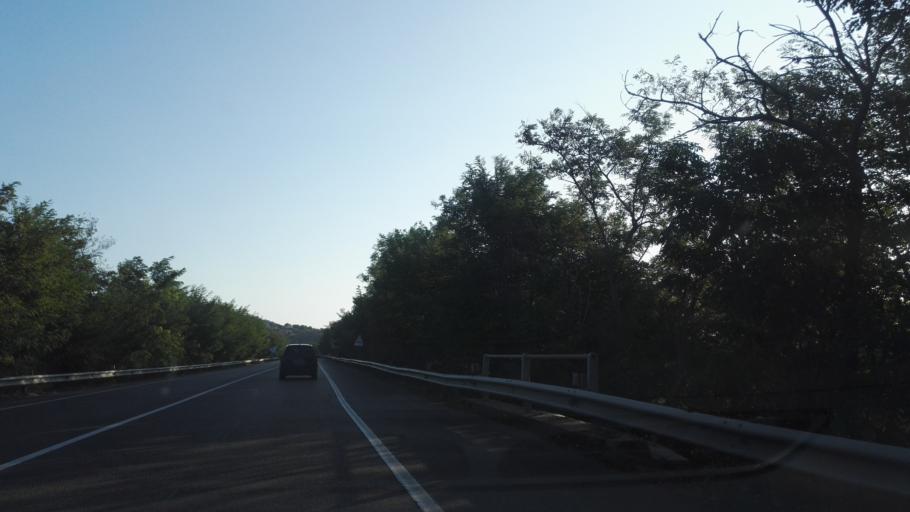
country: IT
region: Calabria
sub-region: Provincia di Catanzaro
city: Montepaone Lido
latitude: 38.7338
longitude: 16.5423
